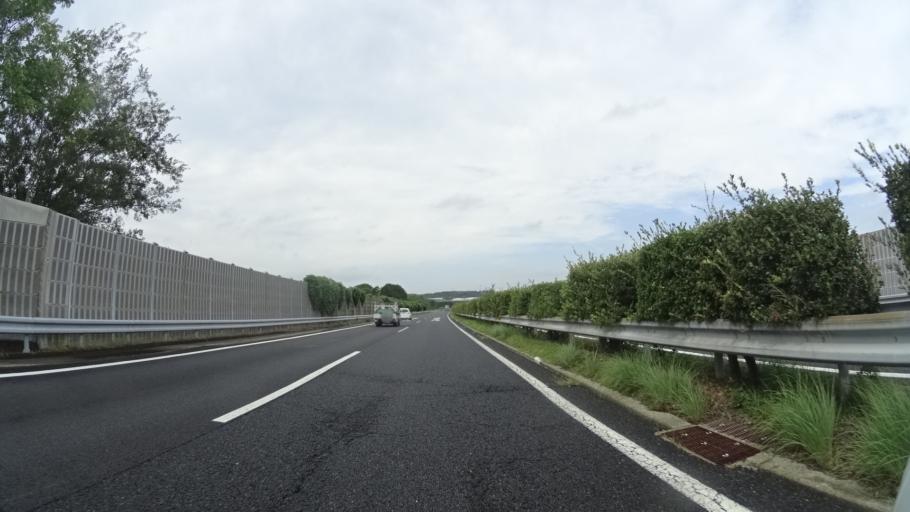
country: JP
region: Hyogo
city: Yashiro
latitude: 34.9289
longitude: 134.9528
